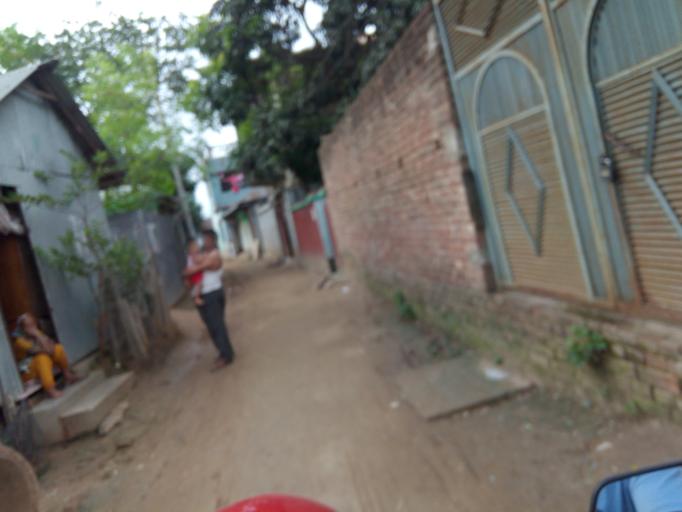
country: BD
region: Dhaka
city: Paltan
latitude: 23.7469
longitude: 90.4524
